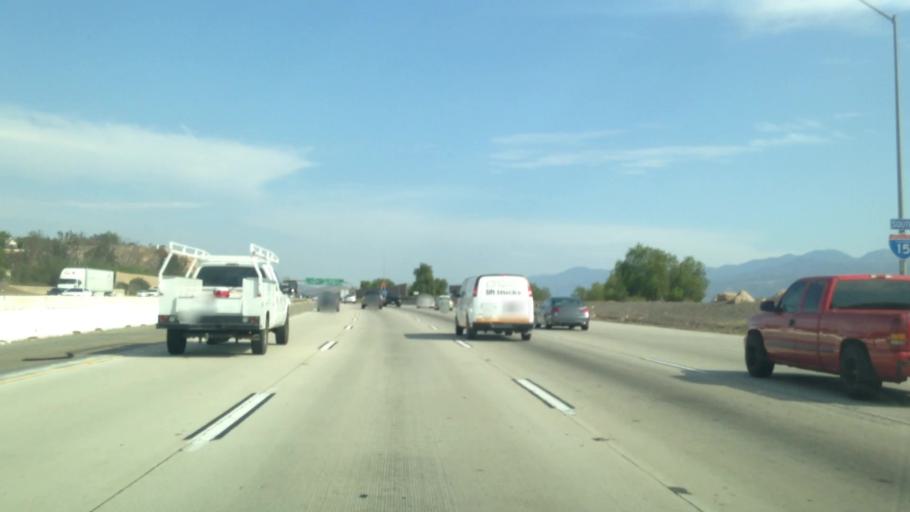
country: US
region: California
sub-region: Riverside County
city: Corona
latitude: 33.8946
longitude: -117.5582
